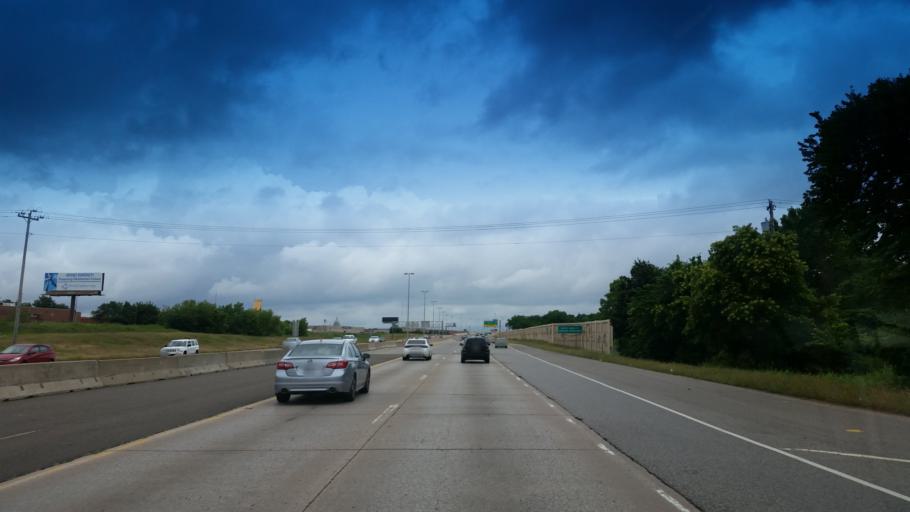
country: US
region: Oklahoma
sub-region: Oklahoma County
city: Nichols Hills
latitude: 35.5157
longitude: -97.5167
